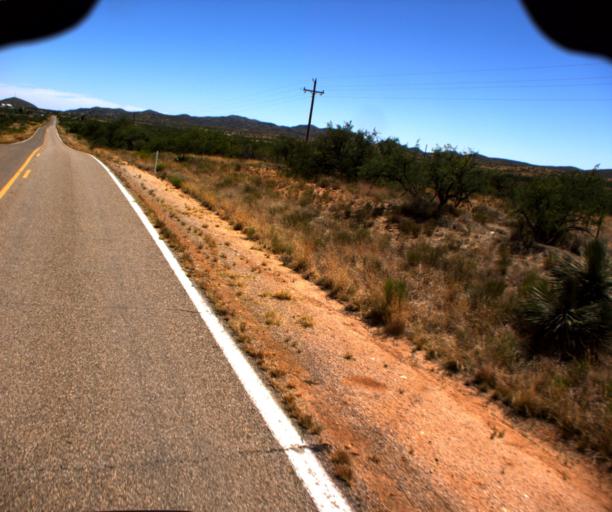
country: US
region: Arizona
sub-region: Santa Cruz County
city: Tubac
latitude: 31.5087
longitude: -111.5458
